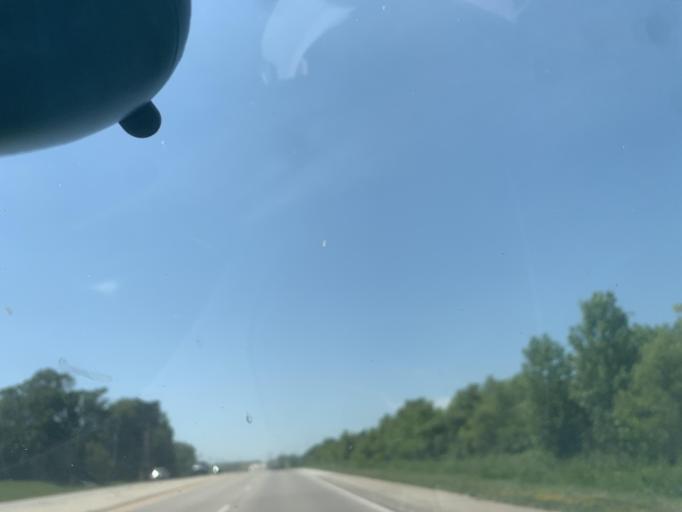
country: US
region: Nebraska
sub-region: Douglas County
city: Elkhorn
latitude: 41.2340
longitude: -96.2228
